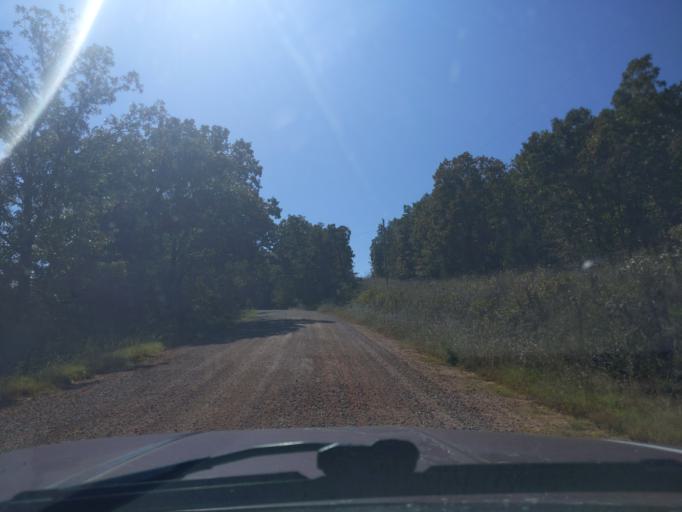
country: US
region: Oklahoma
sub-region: Creek County
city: Bristow
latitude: 35.6791
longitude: -96.4234
